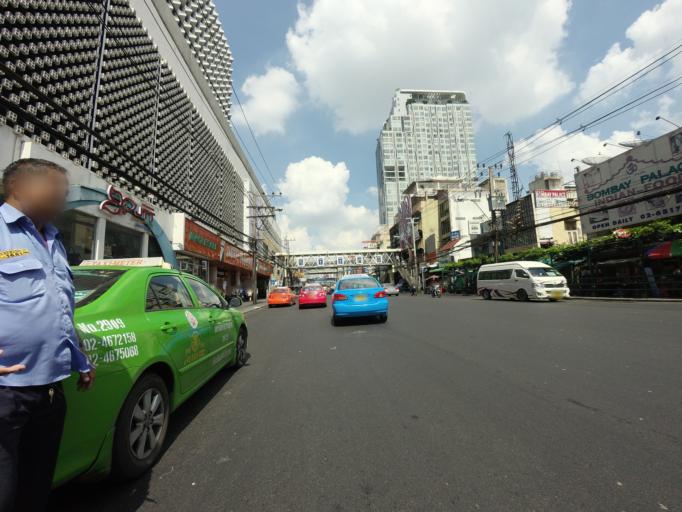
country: TH
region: Bangkok
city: Ratchathewi
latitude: 13.7530
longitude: 100.5417
